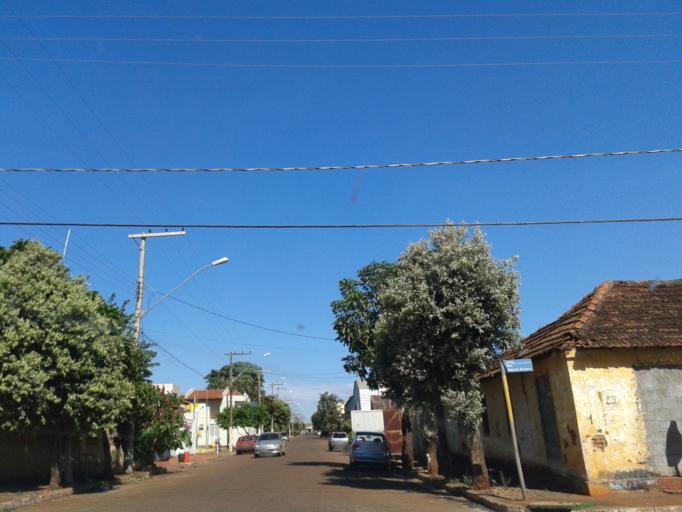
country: BR
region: Minas Gerais
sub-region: Centralina
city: Centralina
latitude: -18.5859
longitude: -49.1969
